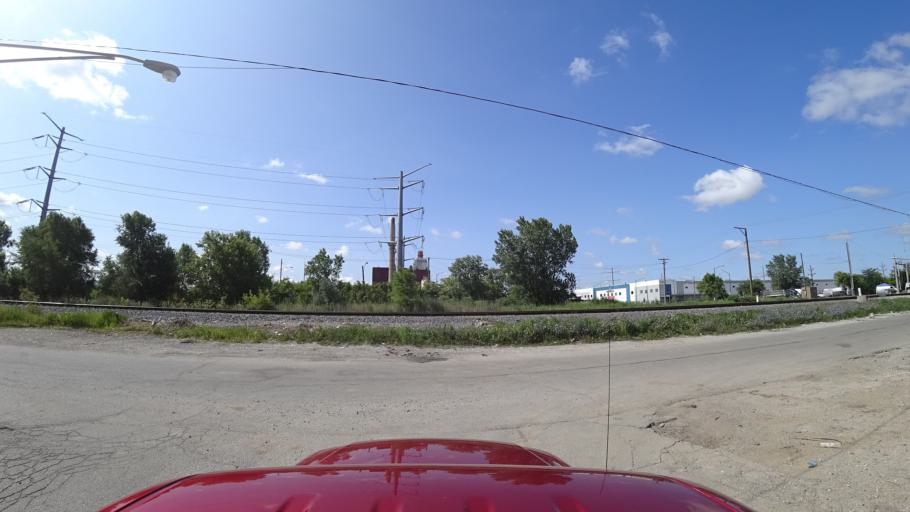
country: US
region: Illinois
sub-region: Cook County
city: Cicero
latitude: 41.8334
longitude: -87.7231
